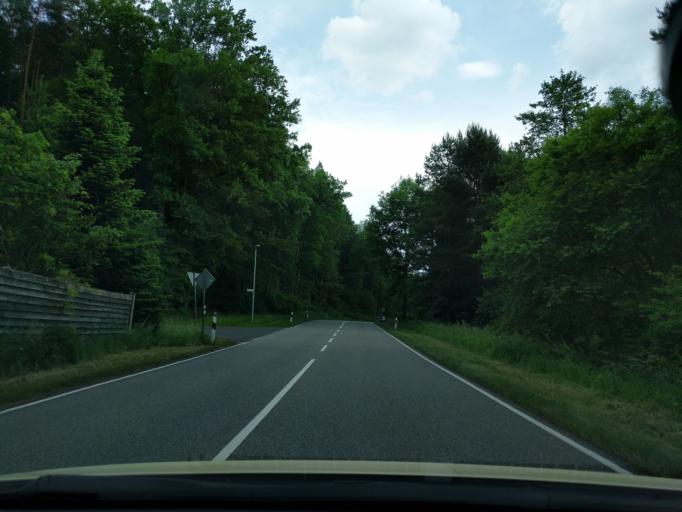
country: DE
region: Rheinland-Pfalz
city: Stelzenberg
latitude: 49.3867
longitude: 7.7005
